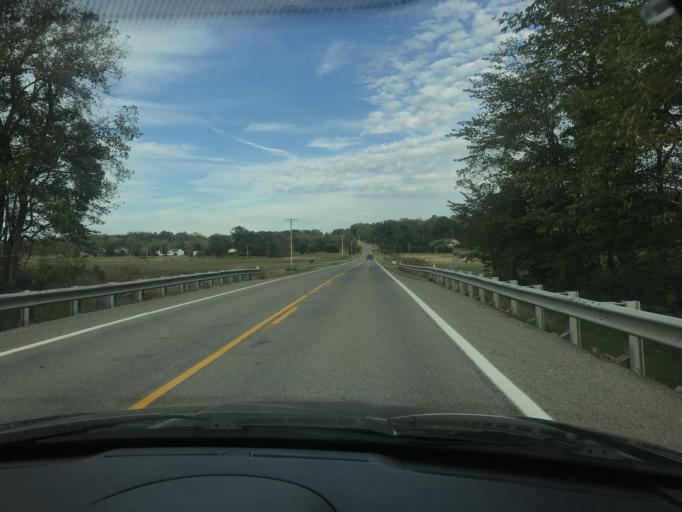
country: US
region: Ohio
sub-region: Logan County
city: West Liberty
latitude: 40.2588
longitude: -83.7048
